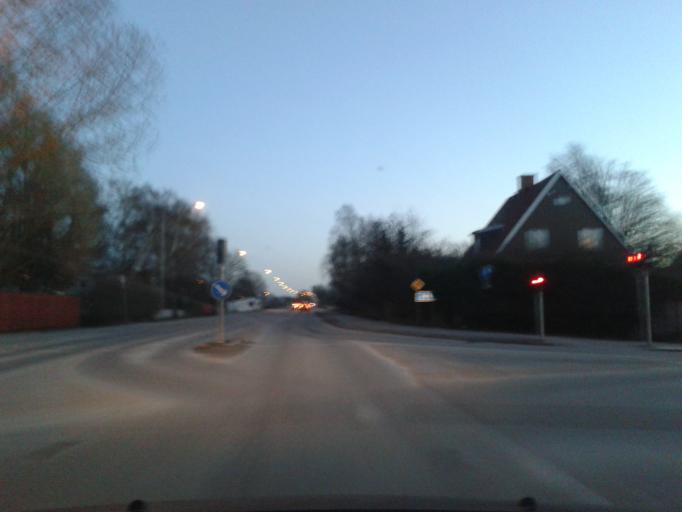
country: SE
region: Gotland
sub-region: Gotland
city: Visby
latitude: 57.6330
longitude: 18.3106
